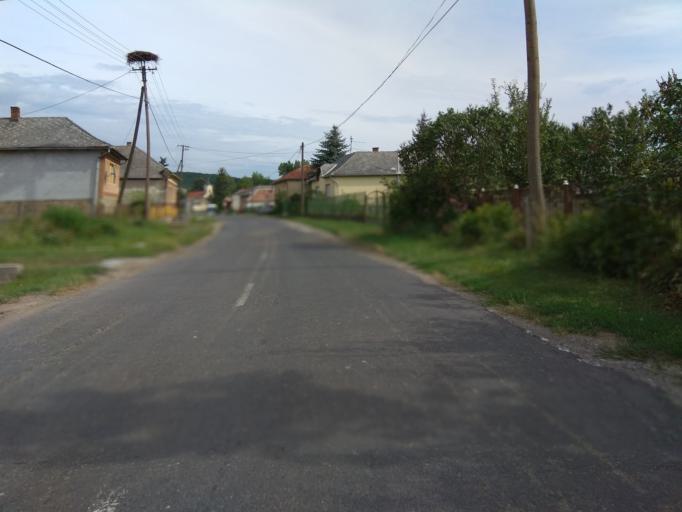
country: HU
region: Heves
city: Tarnalelesz
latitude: 48.0280
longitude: 20.2573
